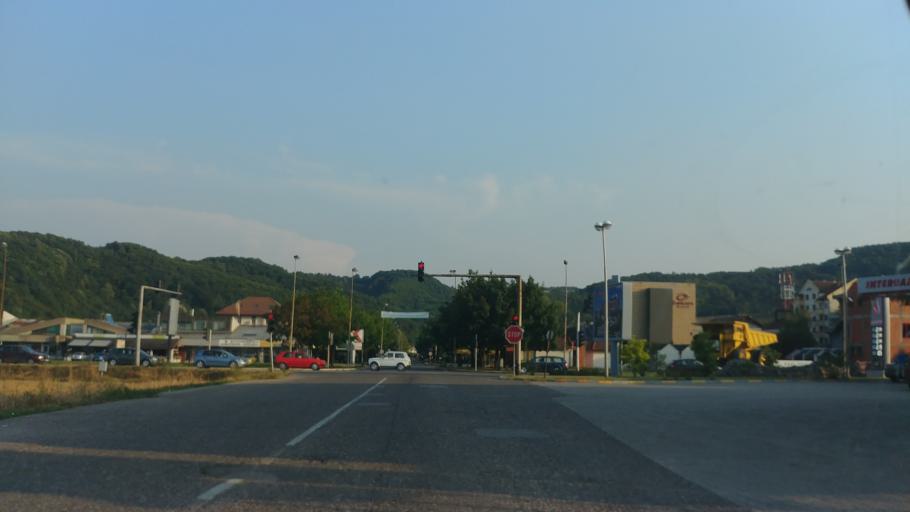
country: BA
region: Republika Srpska
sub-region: Opstina Ugljevik
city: Ugljevik
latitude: 44.6958
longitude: 18.9931
